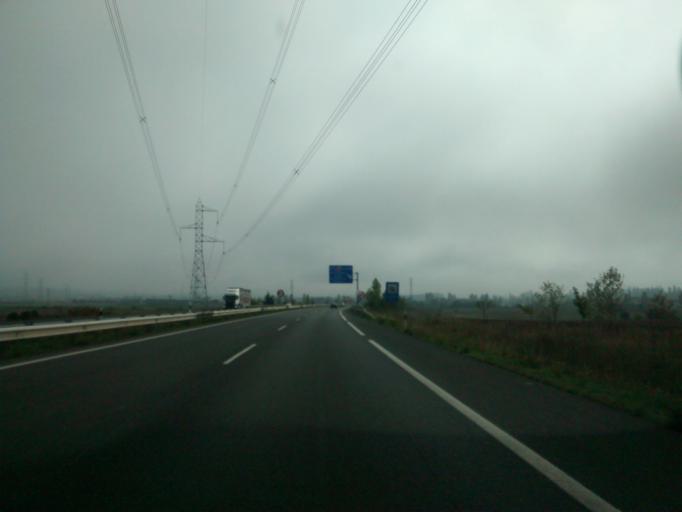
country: ES
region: Basque Country
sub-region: Provincia de Alava
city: Gasteiz / Vitoria
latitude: 42.8811
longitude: -2.6689
